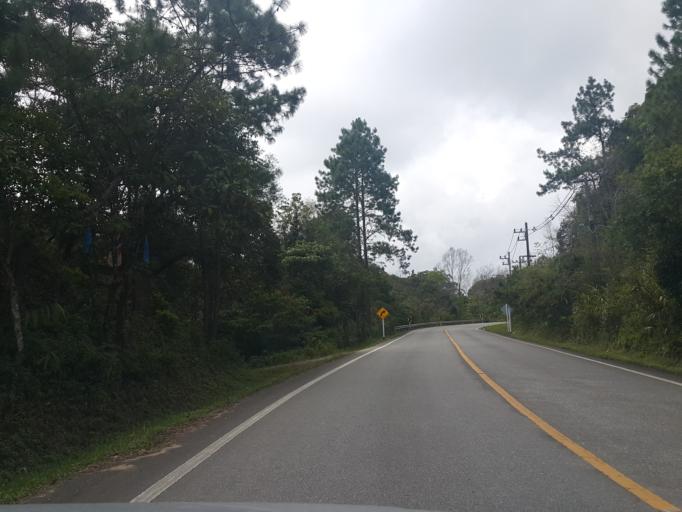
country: TH
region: Chiang Mai
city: Mae Chaem
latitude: 18.5080
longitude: 98.5110
